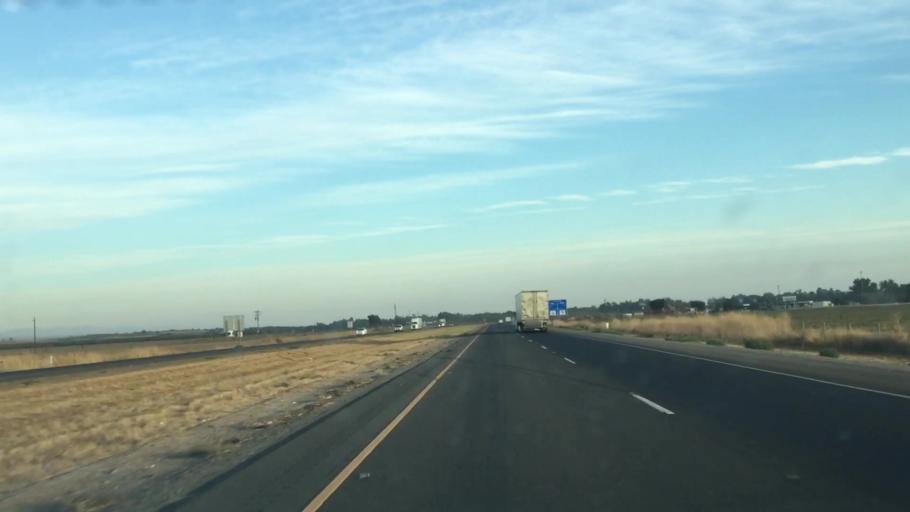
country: US
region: California
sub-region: Yolo County
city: Dunnigan
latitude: 38.8743
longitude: -121.9673
